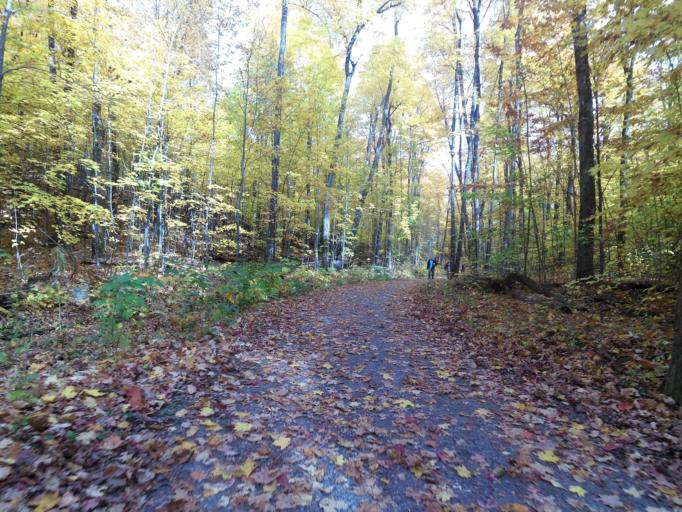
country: CA
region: Quebec
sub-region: Outaouais
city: Gatineau
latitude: 45.4987
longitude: -75.8342
